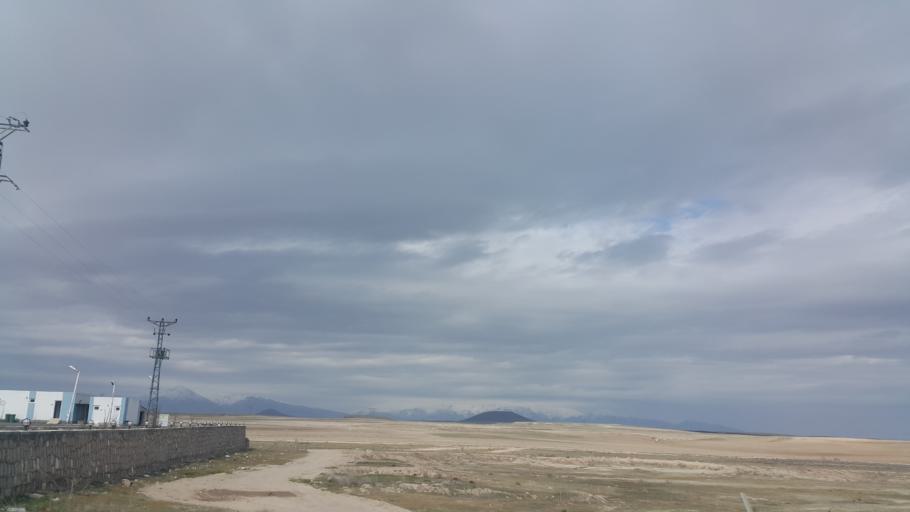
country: TR
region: Nigde
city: Altunhisar
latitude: 37.8860
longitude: 34.1442
